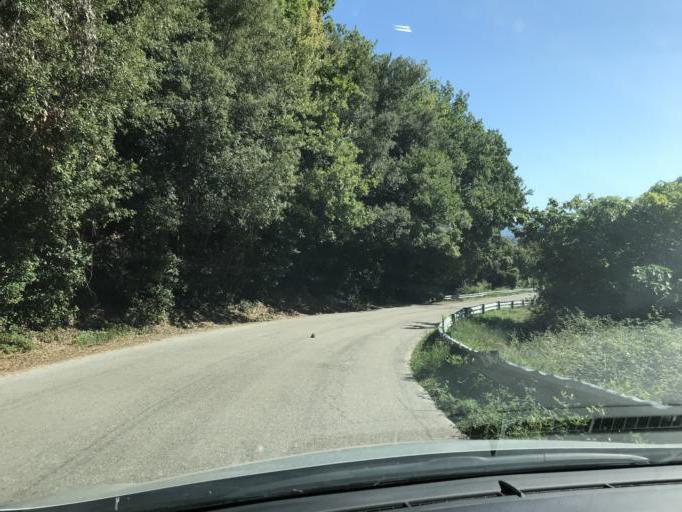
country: IT
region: Umbria
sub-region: Provincia di Terni
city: Avigliano Umbro
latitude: 42.6172
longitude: 12.4076
